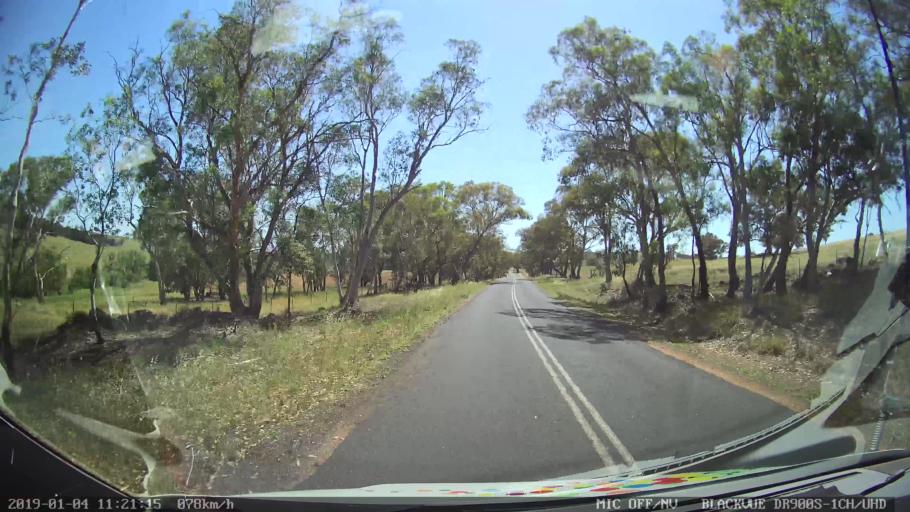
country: AU
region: New South Wales
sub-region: Cabonne
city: Molong
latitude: -33.1558
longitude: 148.7087
